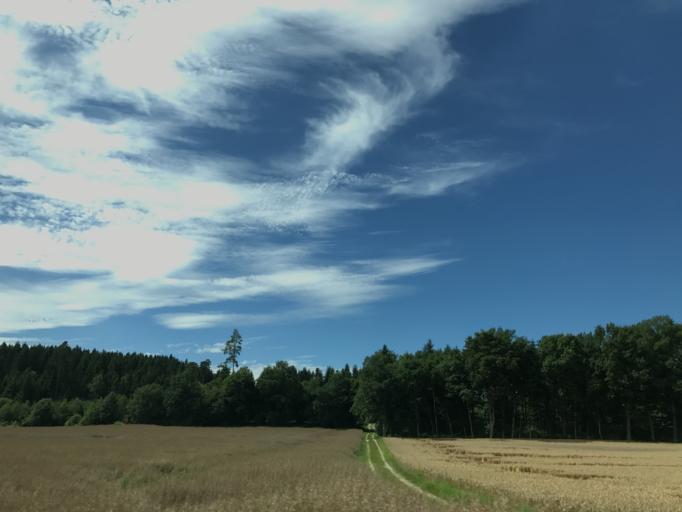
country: DE
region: Baden-Wuerttemberg
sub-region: Tuebingen Region
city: Boms
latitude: 47.9799
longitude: 9.5133
